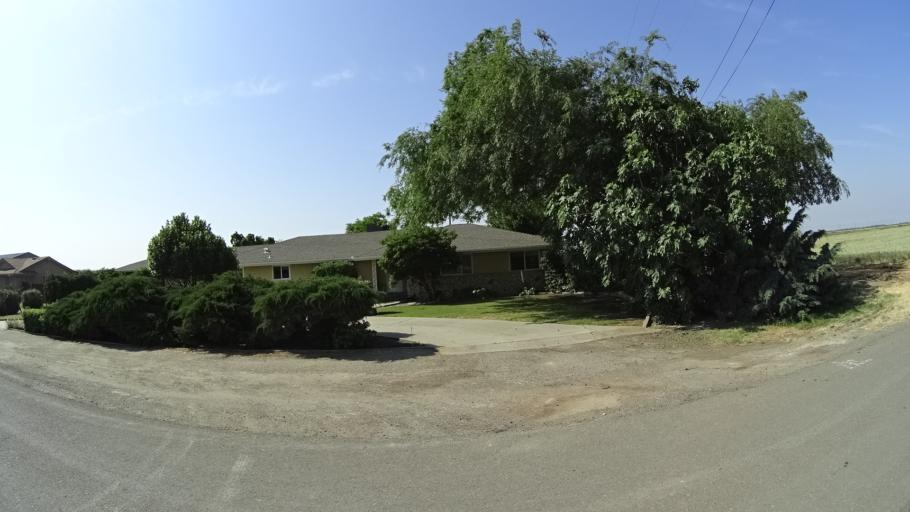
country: US
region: California
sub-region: Kings County
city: Lemoore
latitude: 36.3134
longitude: -119.8171
